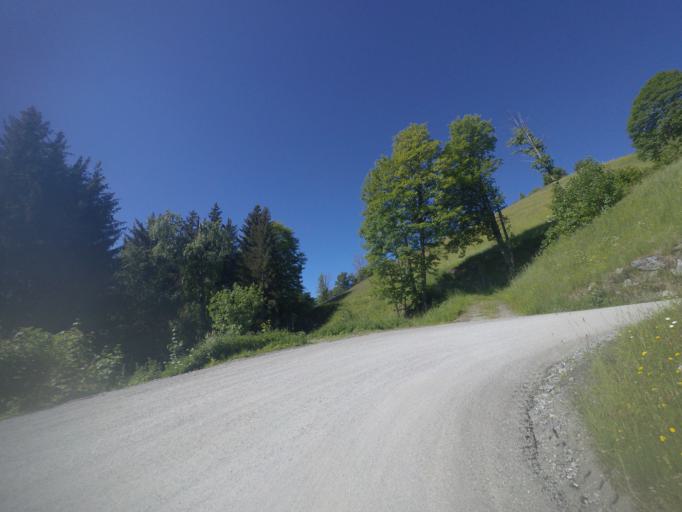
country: AT
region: Salzburg
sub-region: Politischer Bezirk Zell am See
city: Lend
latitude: 47.3271
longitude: 13.0657
